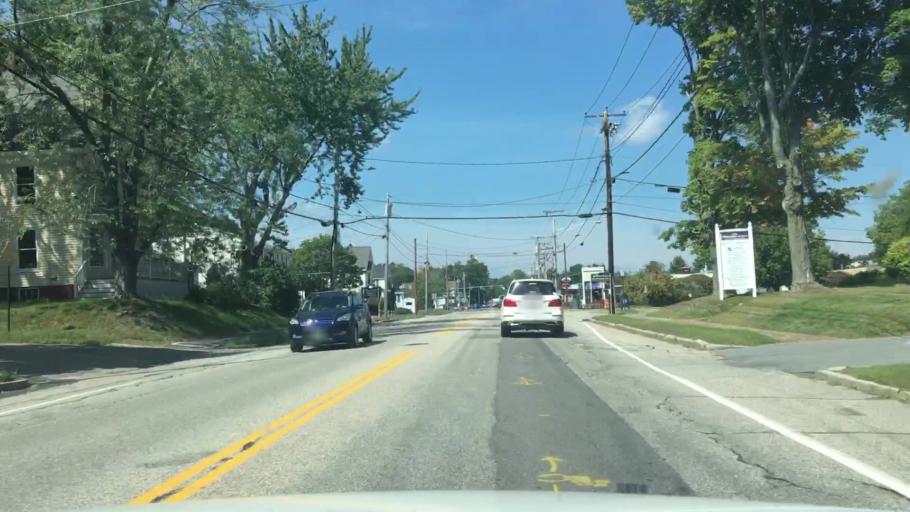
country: US
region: Maine
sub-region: Cumberland County
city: Portland
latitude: 43.6976
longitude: -70.2863
